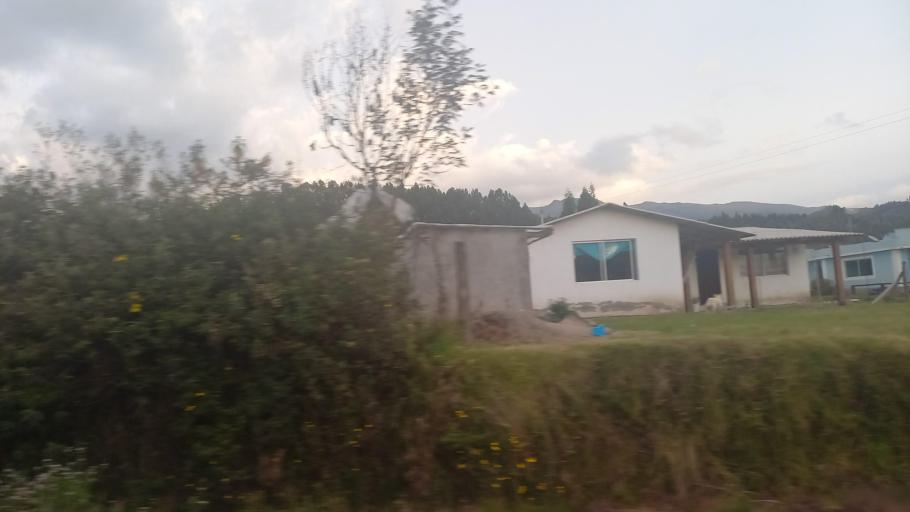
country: EC
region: Pichincha
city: Cayambe
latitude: 0.0805
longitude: -78.1071
